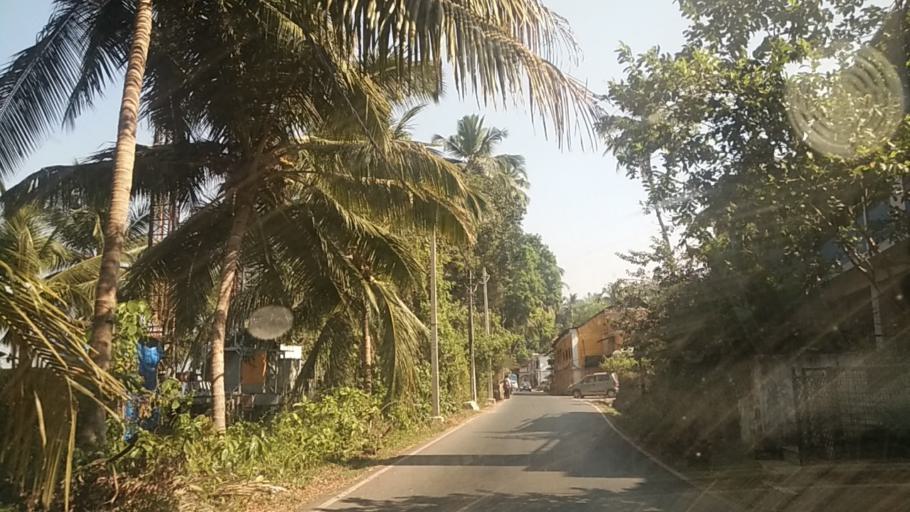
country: IN
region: Goa
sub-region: North Goa
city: Bambolim
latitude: 15.4997
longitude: 73.8800
